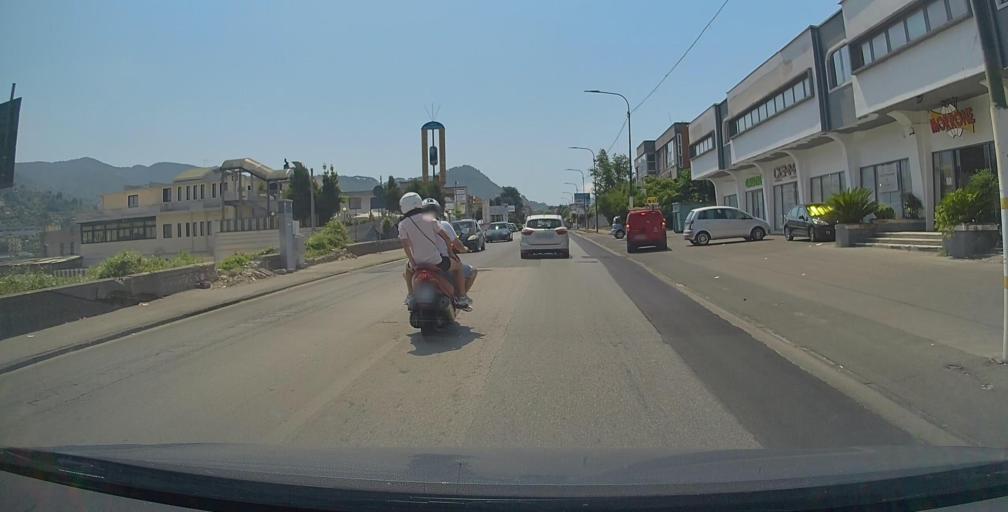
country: IT
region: Campania
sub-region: Provincia di Salerno
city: Nocera Superiore
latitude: 40.7258
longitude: 14.6926
